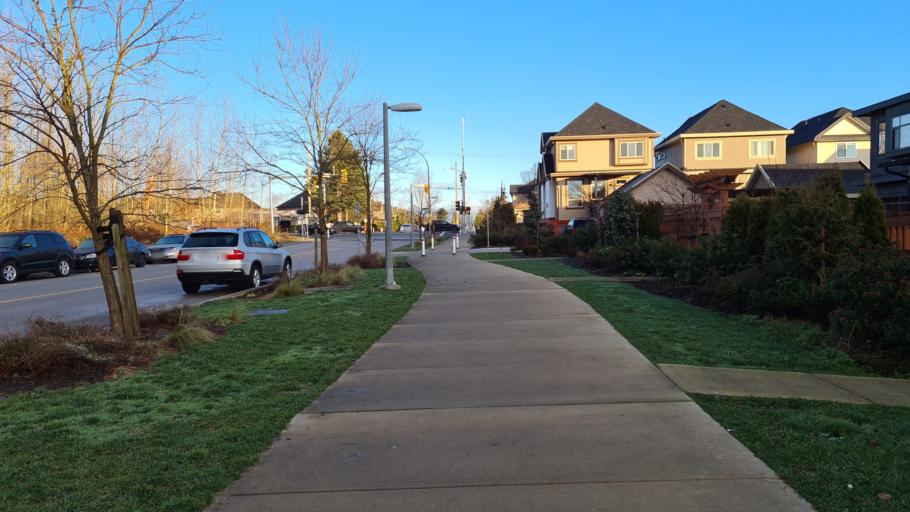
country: CA
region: British Columbia
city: Langley
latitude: 49.1327
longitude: -122.6722
